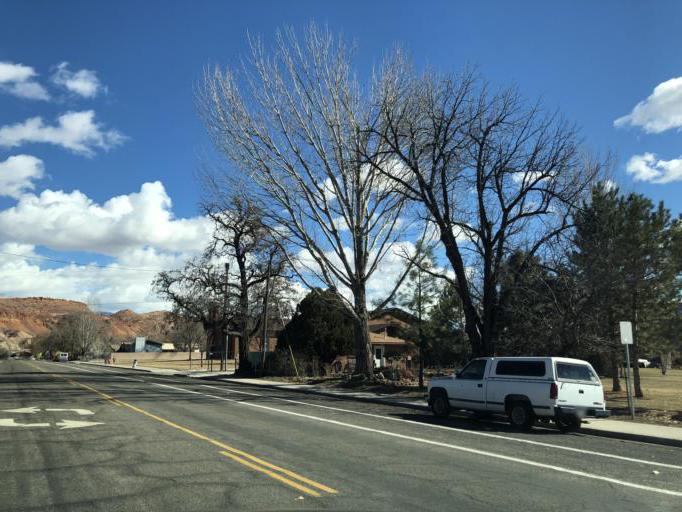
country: US
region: Utah
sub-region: Grand County
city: Moab
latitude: 38.5794
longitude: -109.5595
